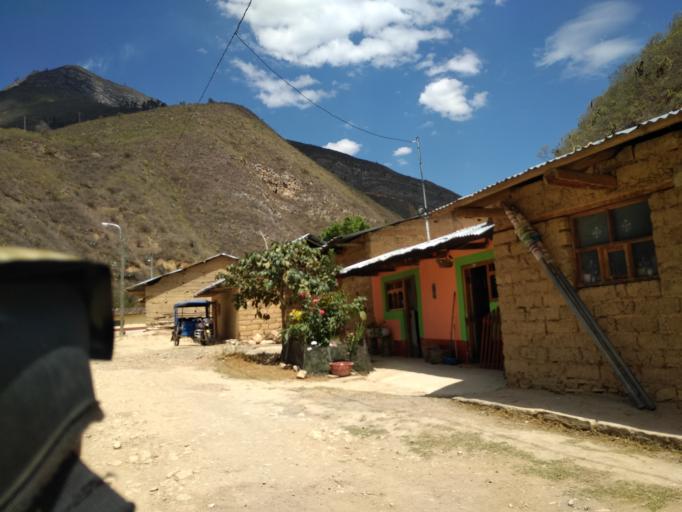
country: PE
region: Amazonas
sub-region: Provincia de Chachapoyas
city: Duraznopampa
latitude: -6.5590
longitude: -77.8292
